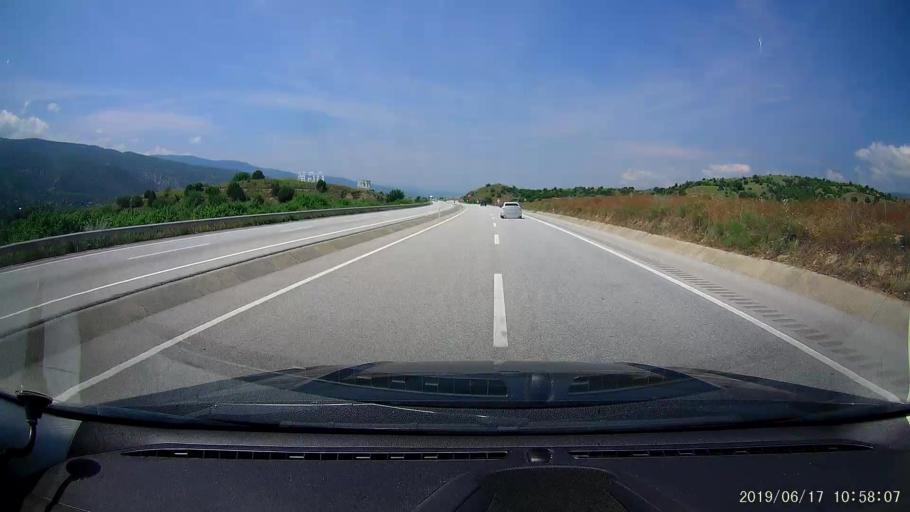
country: TR
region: Kastamonu
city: Tosya
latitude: 41.0463
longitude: 34.2320
